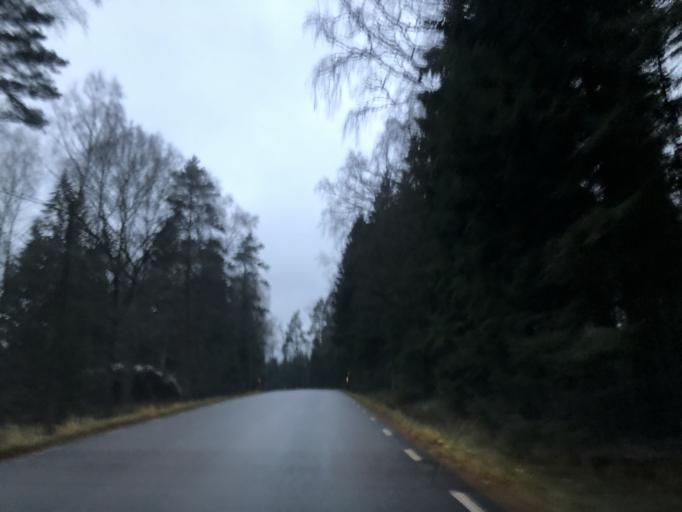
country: SE
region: Vaestra Goetaland
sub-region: Ulricehamns Kommun
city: Ulricehamn
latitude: 57.8506
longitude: 13.2573
